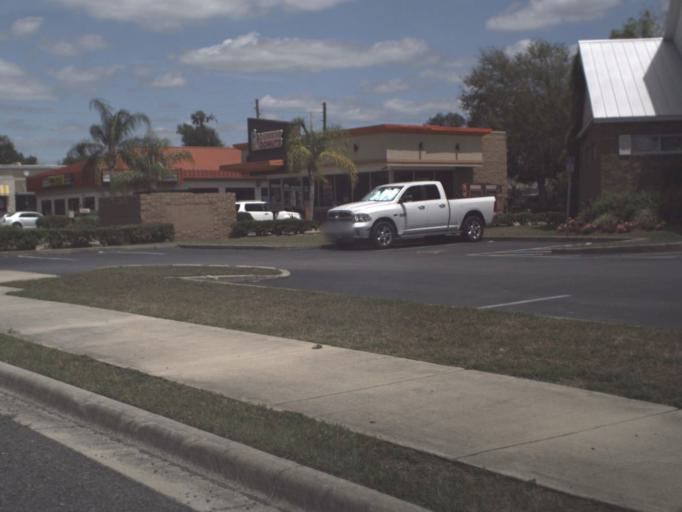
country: US
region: Florida
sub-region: Marion County
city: Ocala
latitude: 29.1469
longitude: -82.1883
